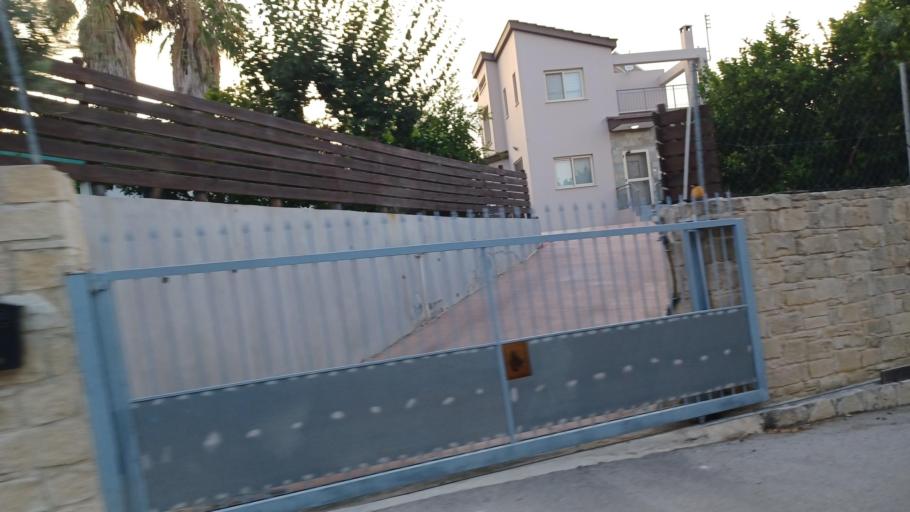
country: CY
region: Pafos
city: Mesogi
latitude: 34.8223
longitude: 32.5817
